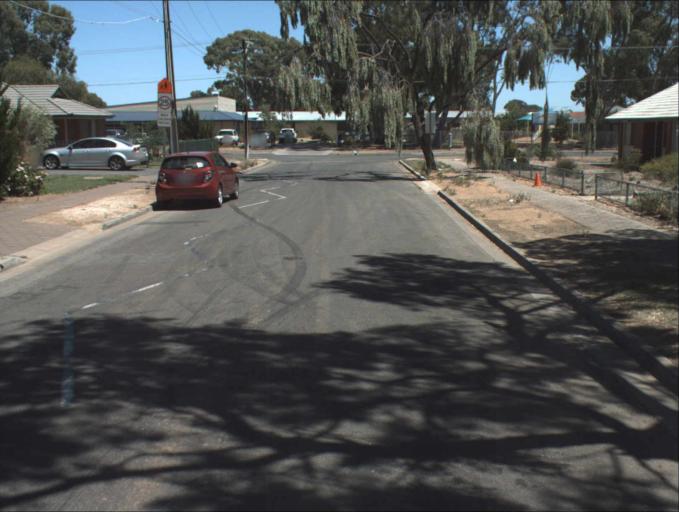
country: AU
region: South Australia
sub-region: Port Adelaide Enfield
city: Klemzig
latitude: -34.8705
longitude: 138.6282
